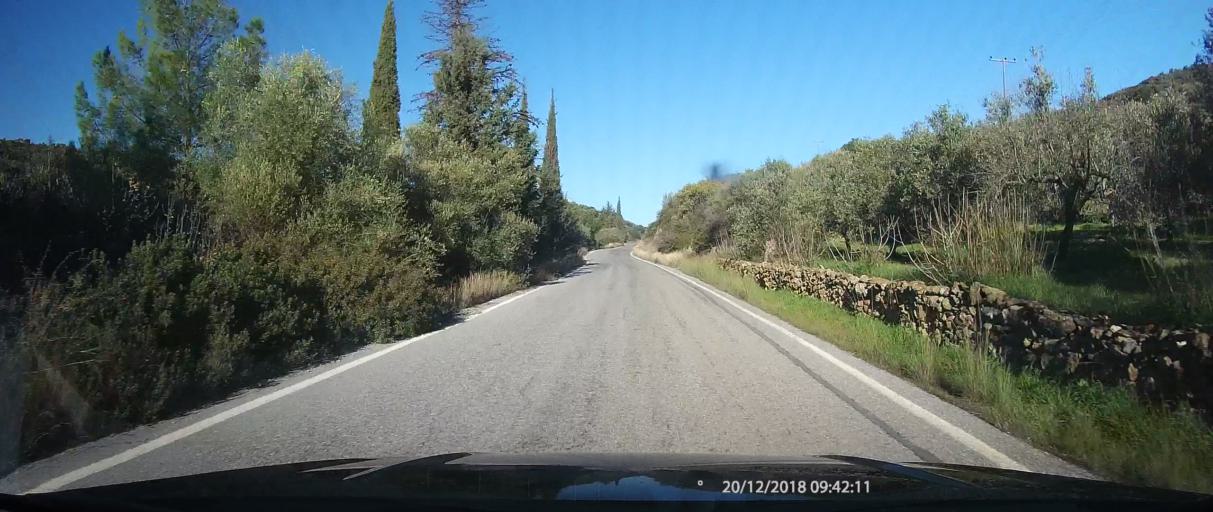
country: GR
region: Peloponnese
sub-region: Nomos Lakonias
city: Yerakion
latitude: 36.9569
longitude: 22.7578
